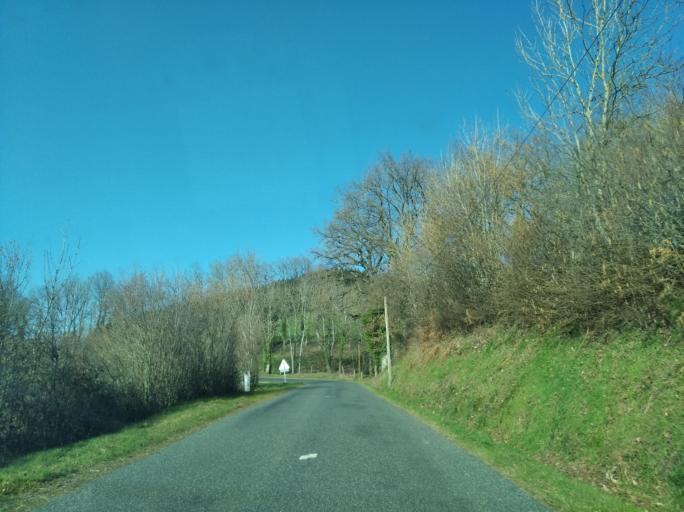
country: FR
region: Auvergne
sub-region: Departement de l'Allier
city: Le Mayet-de-Montagne
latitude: 46.0989
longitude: 3.6808
